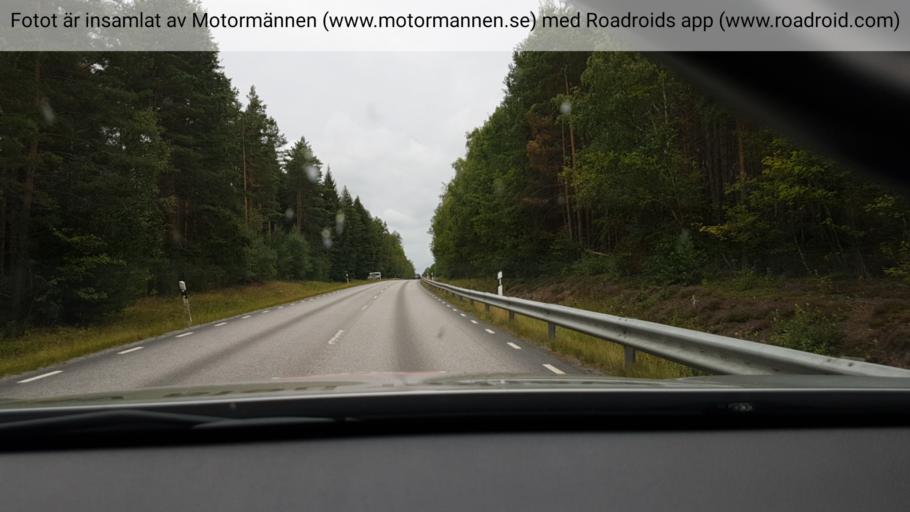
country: SE
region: Stockholm
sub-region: Vallentuna Kommun
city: Vallentuna
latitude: 59.7102
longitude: 18.0511
